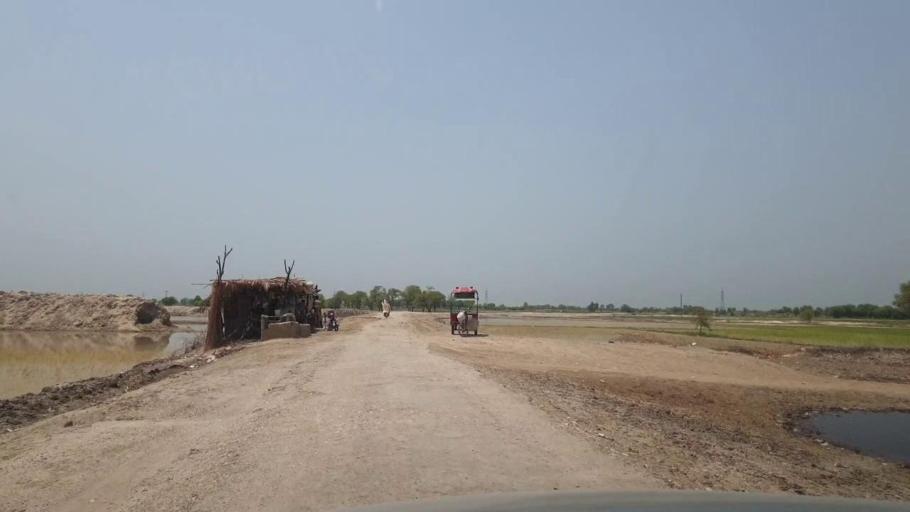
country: PK
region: Sindh
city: Garhi Yasin
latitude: 27.8701
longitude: 68.4539
